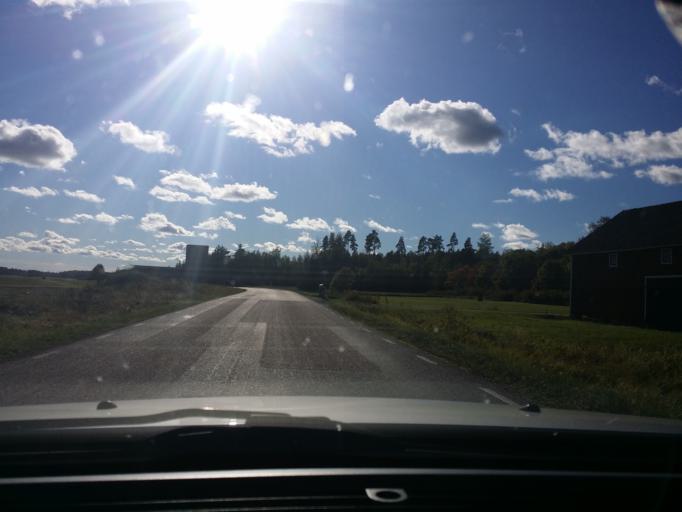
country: SE
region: Vaestmanland
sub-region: Vasteras
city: Vasteras
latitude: 59.5600
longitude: 16.4734
